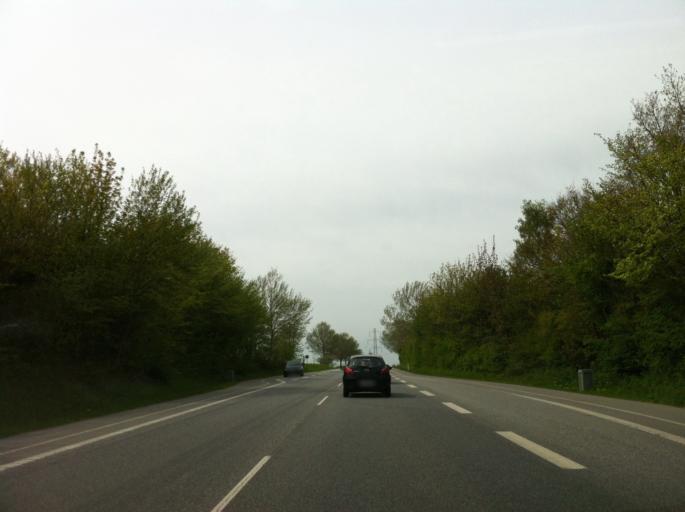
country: DK
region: Capital Region
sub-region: Frederikssund Kommune
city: Slangerup
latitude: 55.8571
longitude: 12.1640
